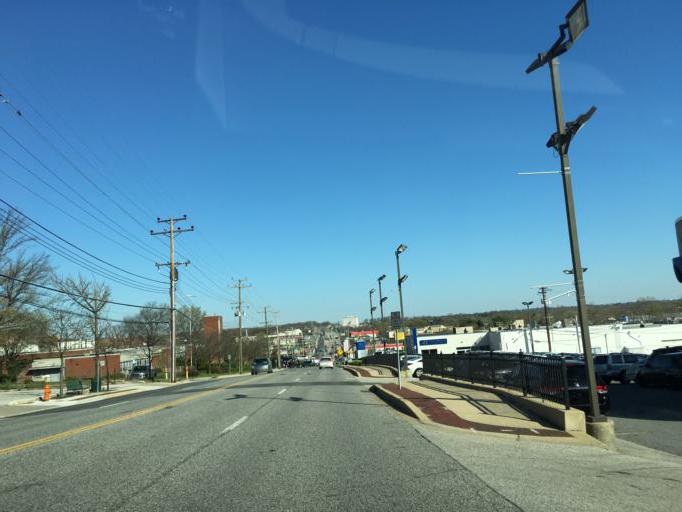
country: US
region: Maryland
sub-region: Baltimore County
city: Towson
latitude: 39.4054
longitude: -76.6055
